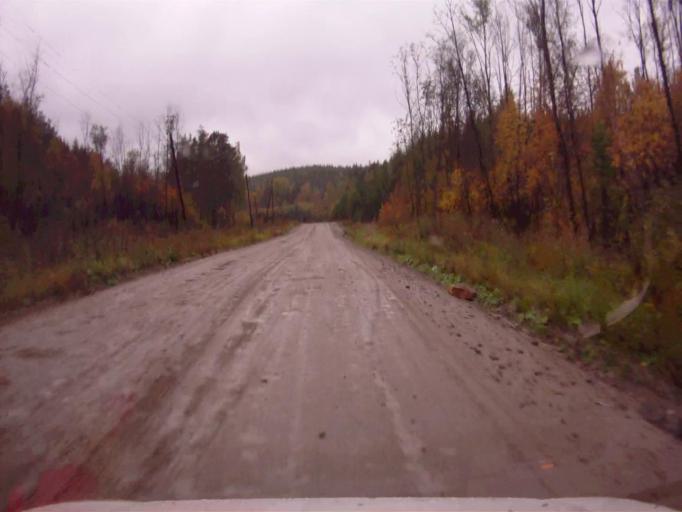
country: RU
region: Chelyabinsk
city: Kyshtym
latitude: 55.7408
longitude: 60.5091
